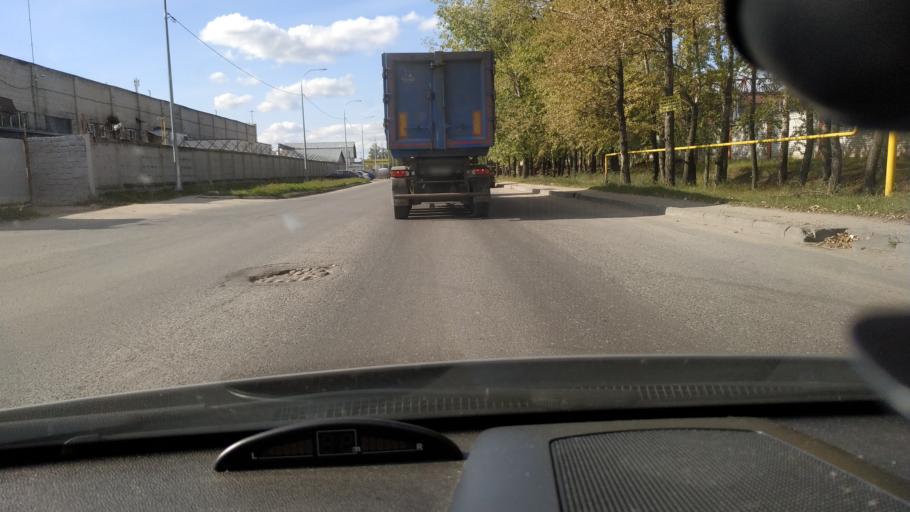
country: RU
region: Rjazan
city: Ryazan'
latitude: 54.6541
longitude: 39.6405
